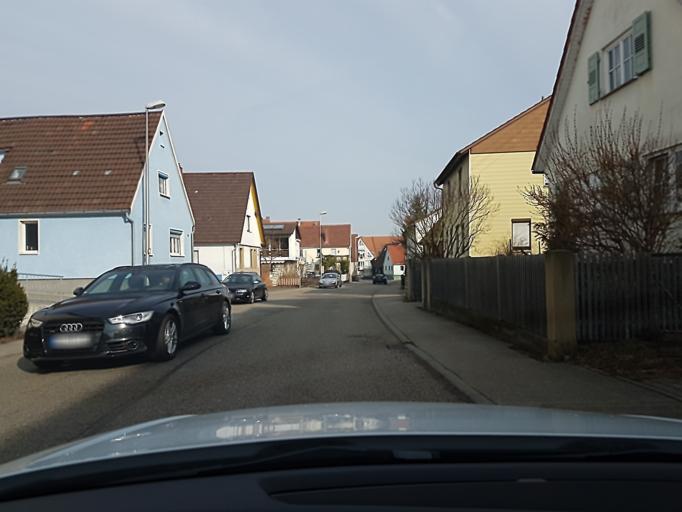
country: DE
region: Baden-Wuerttemberg
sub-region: Regierungsbezirk Stuttgart
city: Leingarten
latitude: 49.1422
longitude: 9.1274
